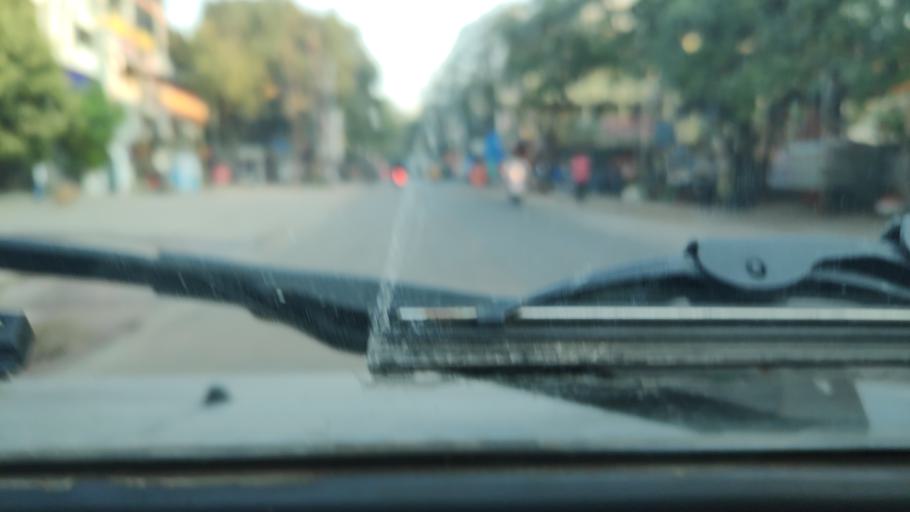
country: IN
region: Telangana
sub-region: Rangareddi
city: Gaddi Annaram
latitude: 17.3637
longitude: 78.5217
